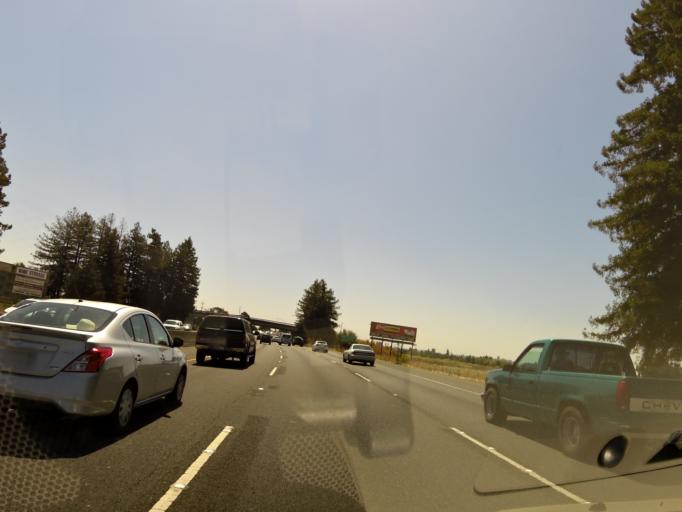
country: US
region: California
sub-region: Sonoma County
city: Rohnert Park
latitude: 38.3734
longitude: -122.7155
